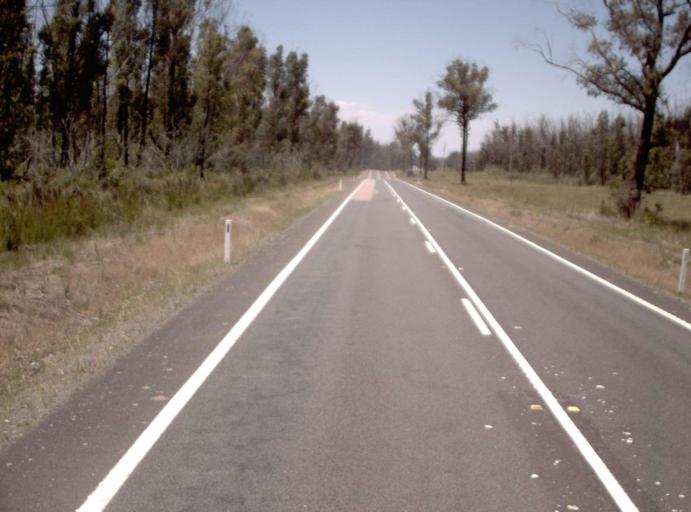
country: AU
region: Victoria
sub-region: East Gippsland
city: Lakes Entrance
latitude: -37.7491
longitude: 148.2313
